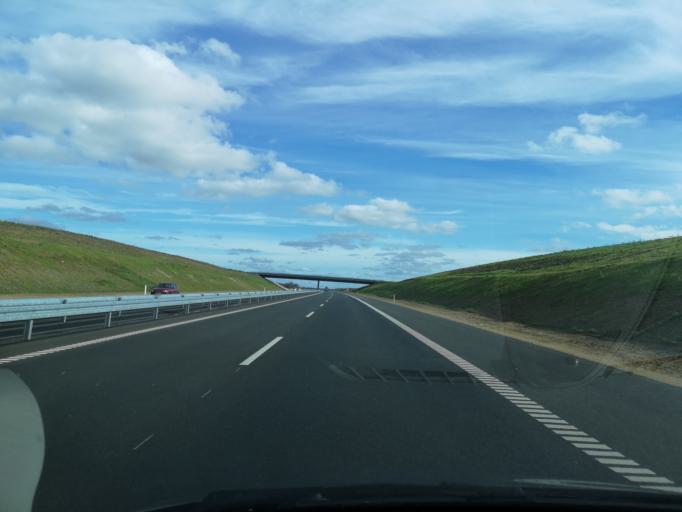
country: DK
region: Central Jutland
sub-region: Holstebro Kommune
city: Holstebro
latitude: 56.3814
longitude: 8.6727
